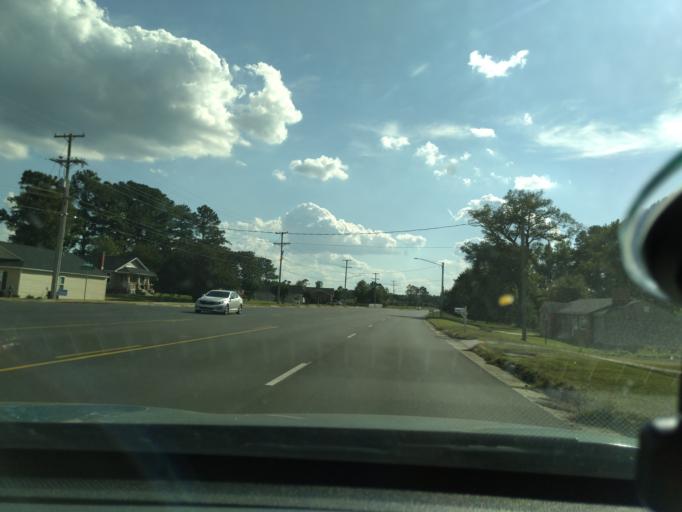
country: US
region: North Carolina
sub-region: Nash County
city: Rocky Mount
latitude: 35.9173
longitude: -77.8270
